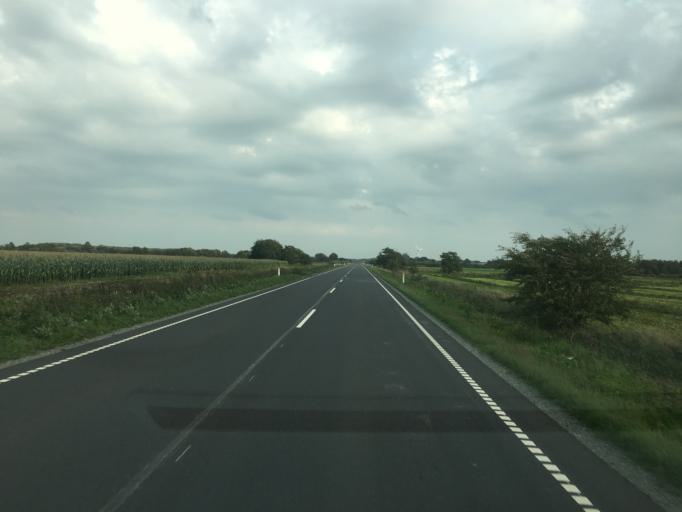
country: DE
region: Schleswig-Holstein
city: Bramstedtlund
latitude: 54.9738
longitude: 9.0619
